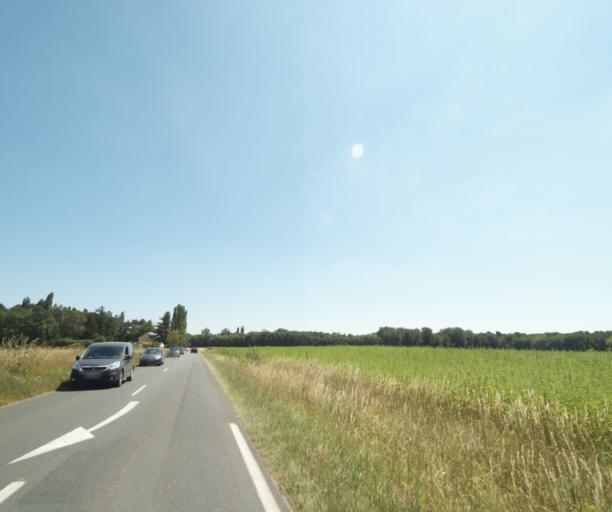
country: FR
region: Ile-de-France
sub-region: Departement de l'Essonne
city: Milly-la-Foret
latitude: 48.3962
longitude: 2.4834
